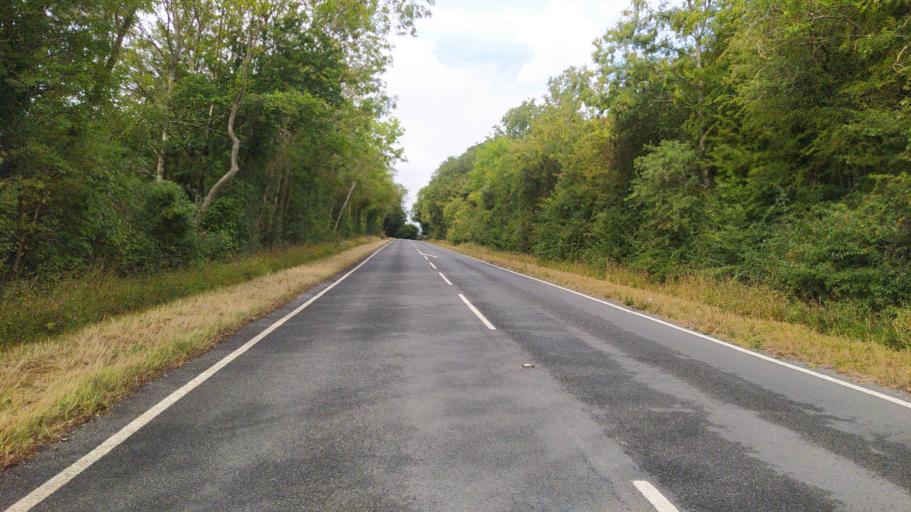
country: GB
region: England
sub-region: Hampshire
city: Petersfield
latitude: 50.9716
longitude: -0.8914
